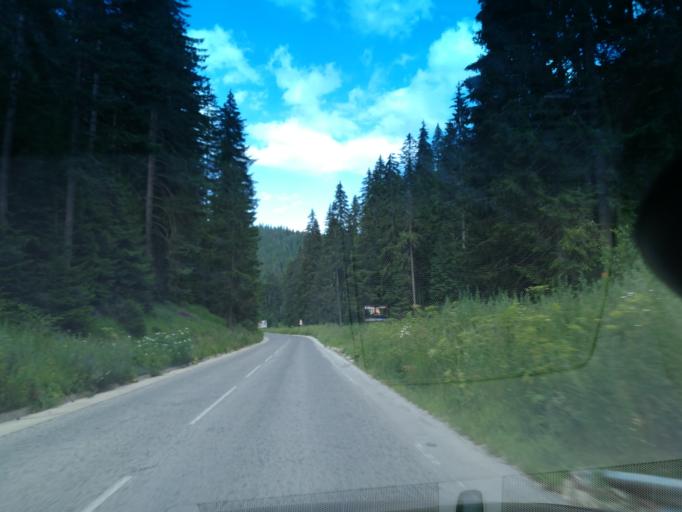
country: BG
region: Smolyan
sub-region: Obshtina Smolyan
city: Smolyan
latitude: 41.6583
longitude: 24.7076
